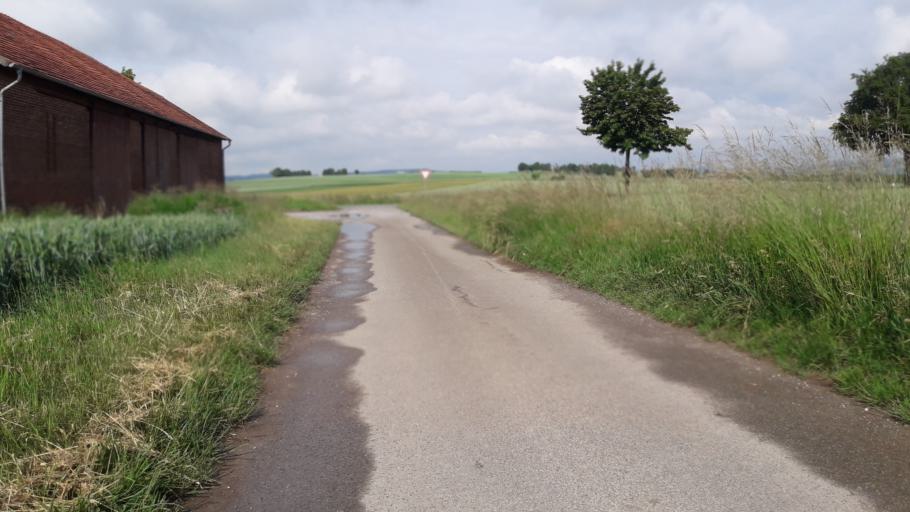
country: DE
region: North Rhine-Westphalia
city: Warburg
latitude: 51.5066
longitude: 9.1293
